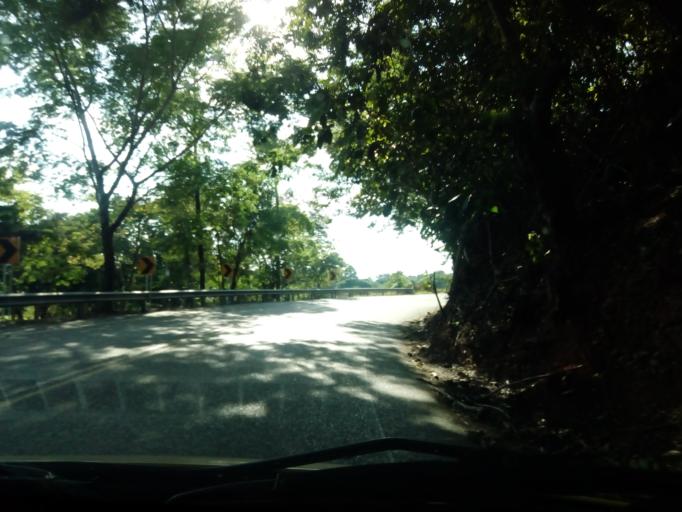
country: CO
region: Boyaca
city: Puerto Boyaca
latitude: 5.9353
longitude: -74.5458
